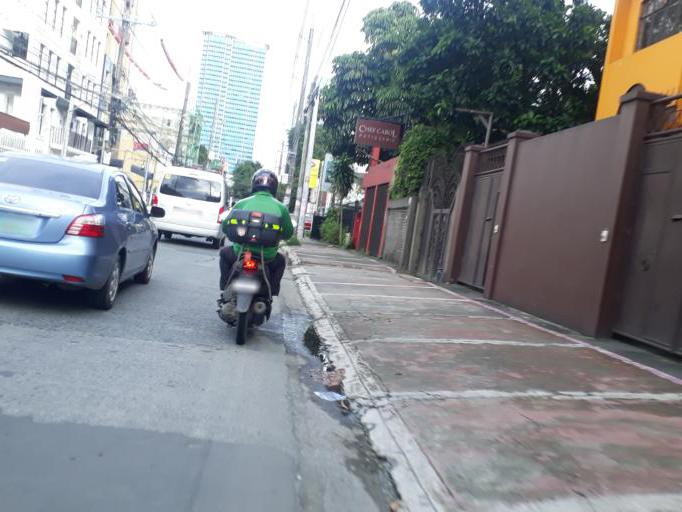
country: PH
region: Metro Manila
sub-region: Quezon City
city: Quezon City
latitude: 14.6353
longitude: 121.0688
